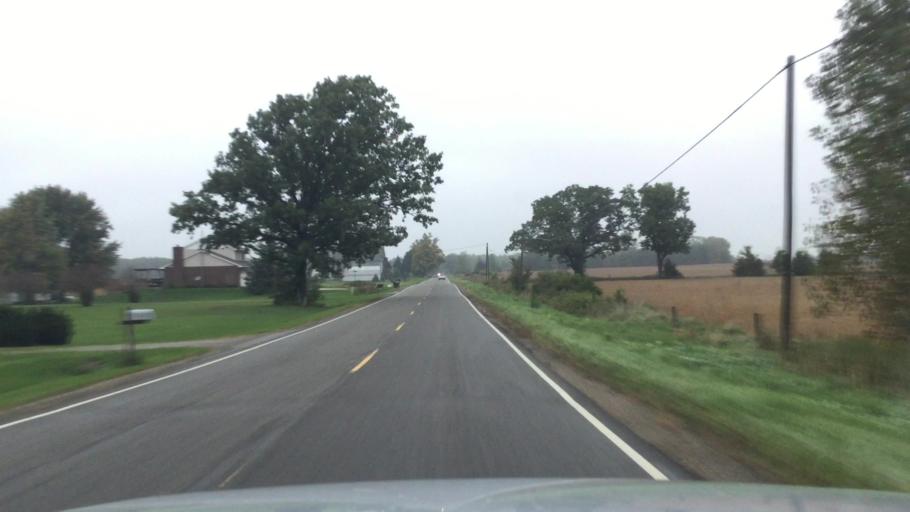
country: US
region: Michigan
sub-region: Shiawassee County
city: Corunna
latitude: 42.9219
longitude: -84.1241
